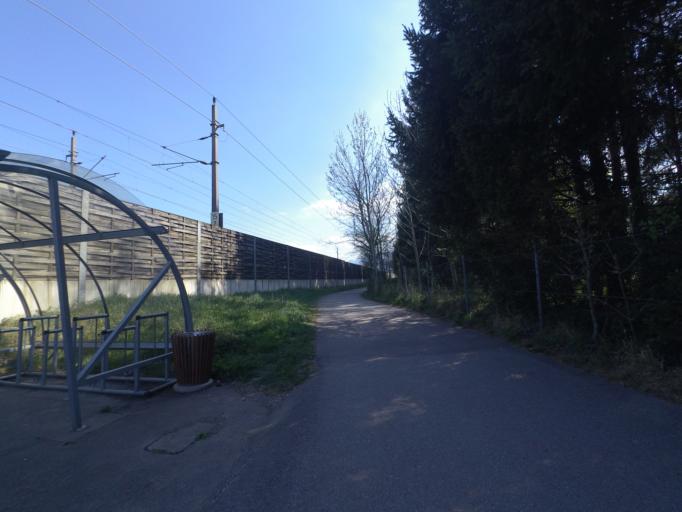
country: AT
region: Salzburg
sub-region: Politischer Bezirk Hallein
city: Puch bei Hallein
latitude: 47.7072
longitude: 13.0922
